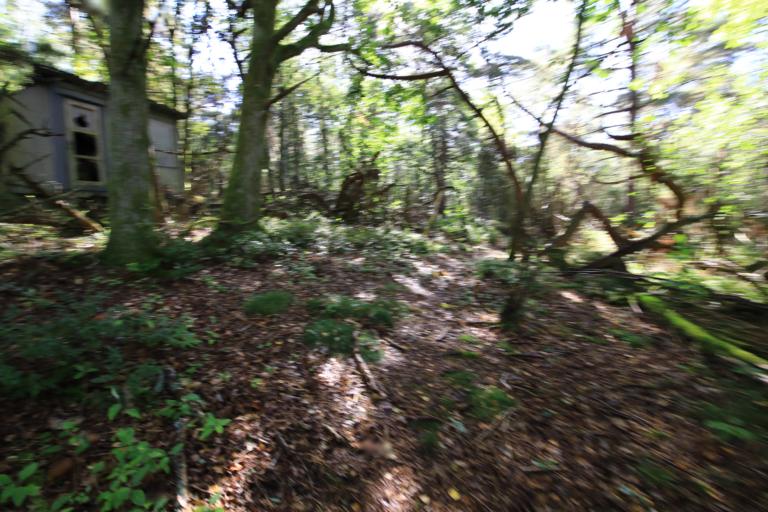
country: SE
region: Halland
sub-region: Varbergs Kommun
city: Varberg
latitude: 57.1797
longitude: 12.2154
